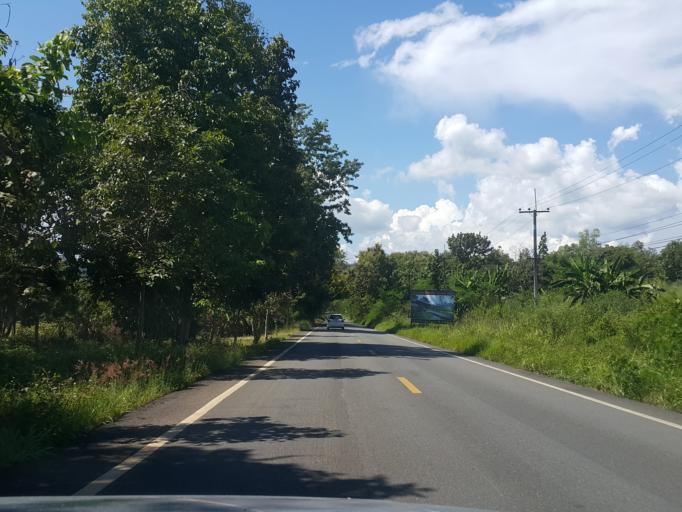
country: TH
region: Chiang Mai
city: Mae Taeng
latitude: 19.1682
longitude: 98.9296
